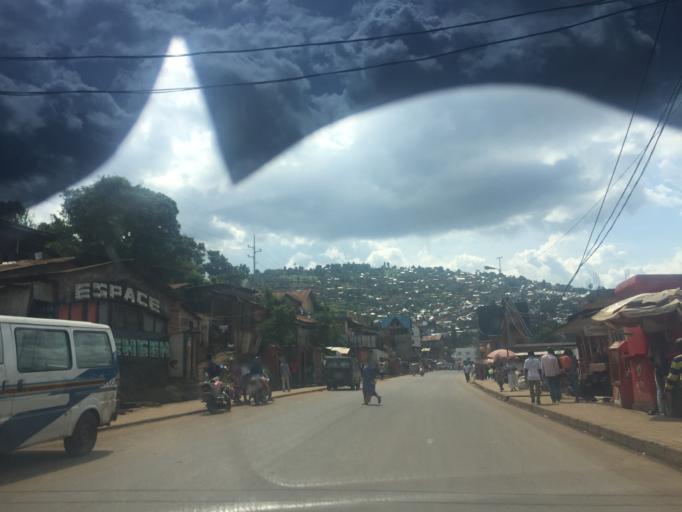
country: CD
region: South Kivu
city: Bukavu
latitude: -2.4836
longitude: 28.8421
